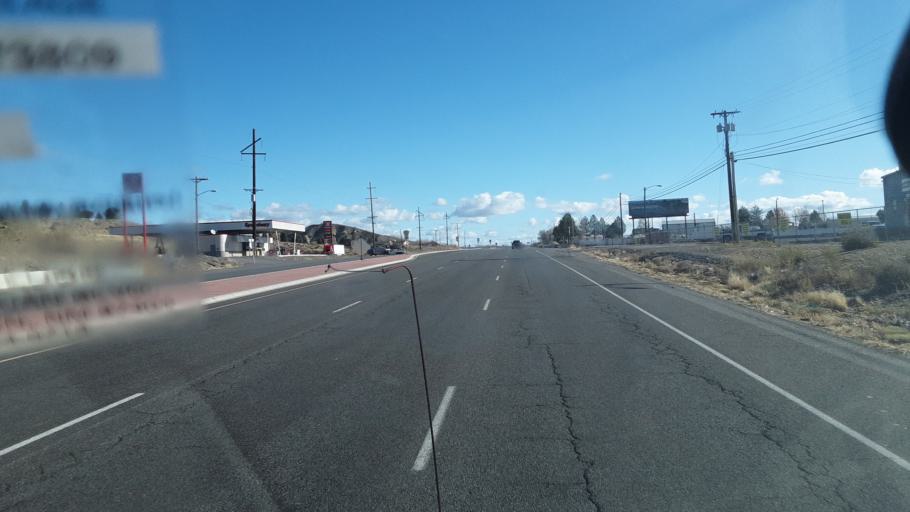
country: US
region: New Mexico
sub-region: San Juan County
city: Lee Acres
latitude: 36.7054
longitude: -108.0228
